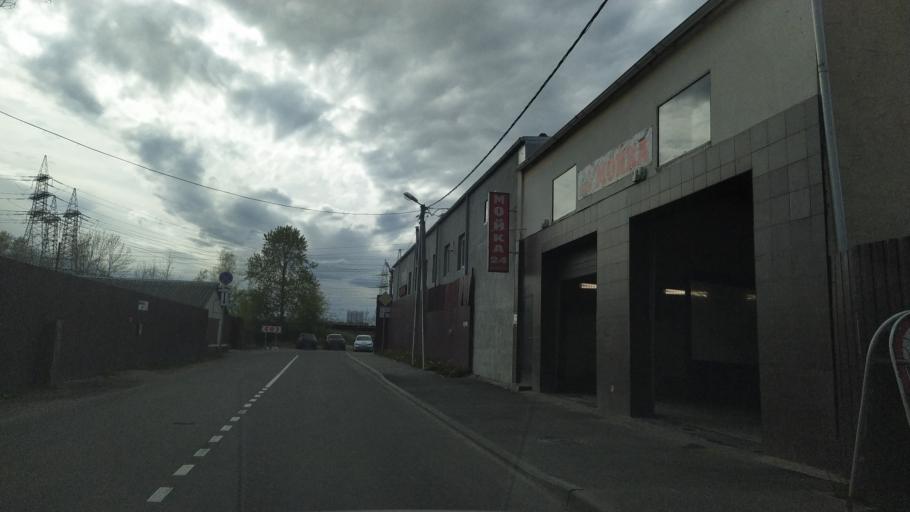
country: RU
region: Leningrad
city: Murino
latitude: 60.0450
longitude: 30.4414
